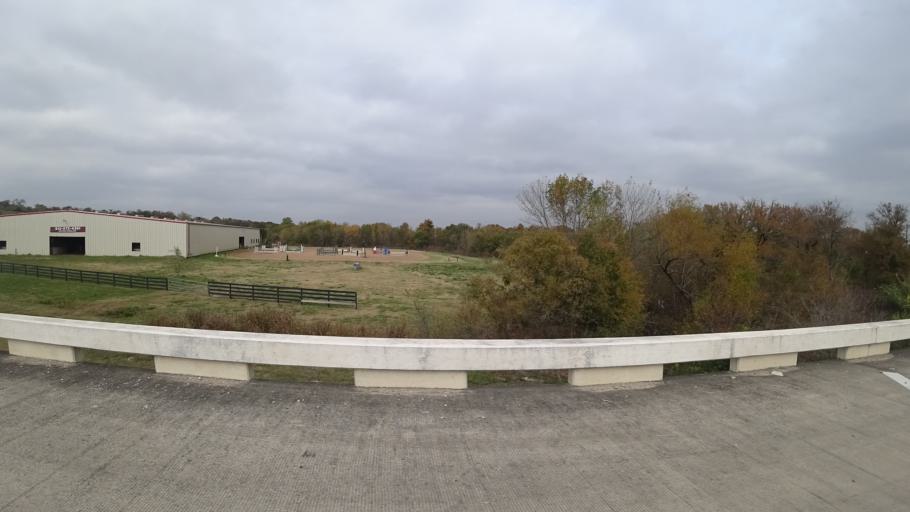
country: US
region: Texas
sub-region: Travis County
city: Pflugerville
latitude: 30.3833
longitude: -97.6025
